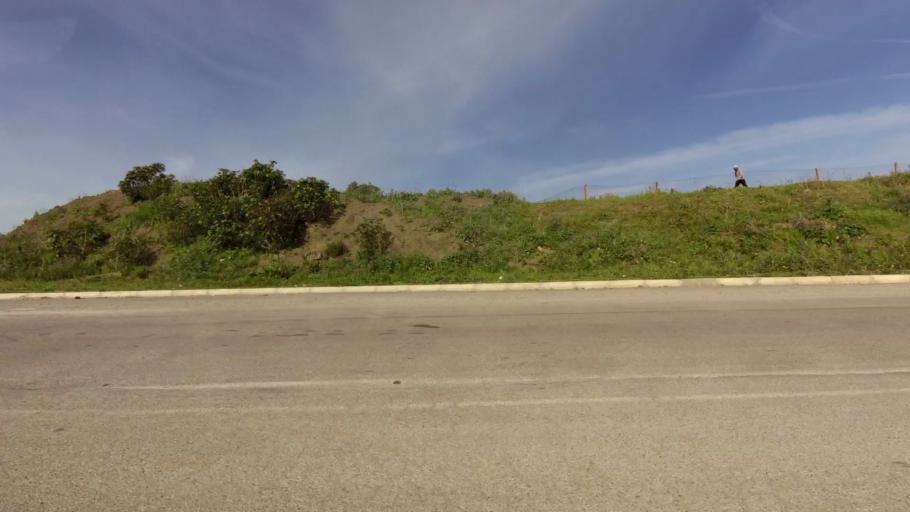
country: MA
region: Tanger-Tetouan
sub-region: Tanger-Assilah
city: Tangier
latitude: 35.7069
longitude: -5.8060
